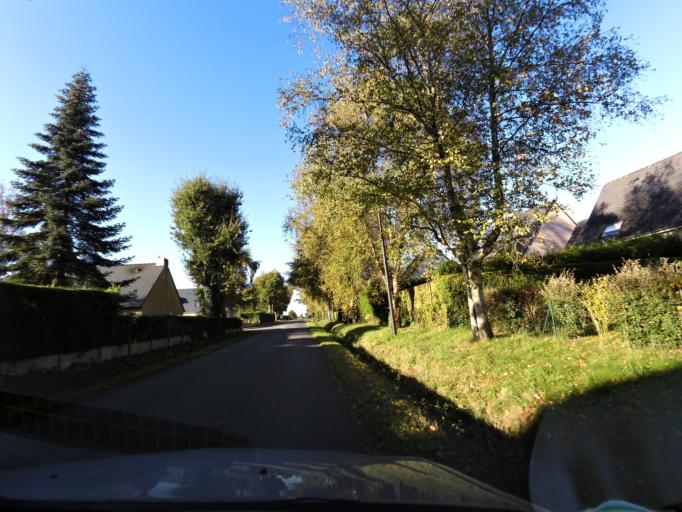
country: FR
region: Brittany
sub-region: Departement d'Ille-et-Vilaine
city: Crevin
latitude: 47.9391
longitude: -1.6521
